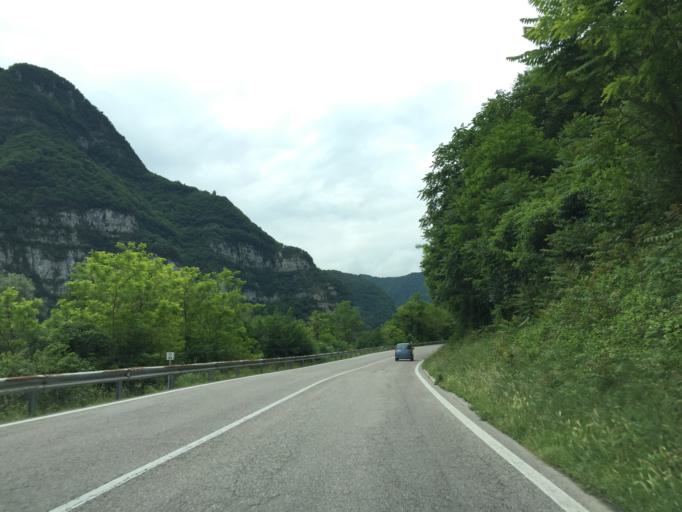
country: IT
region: Veneto
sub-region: Provincia di Belluno
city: Vas
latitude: 45.9582
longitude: 11.9336
